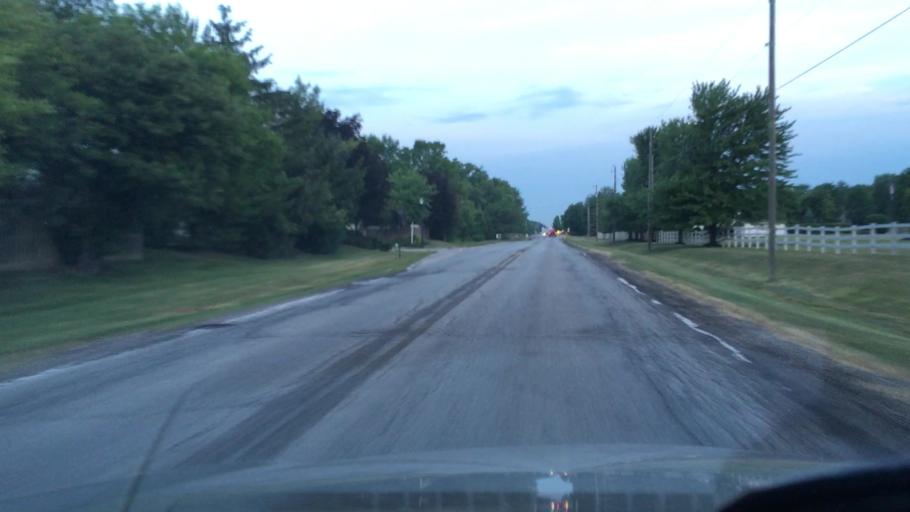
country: US
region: Indiana
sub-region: Marion County
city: Lawrence
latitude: 39.8907
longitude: -86.0350
